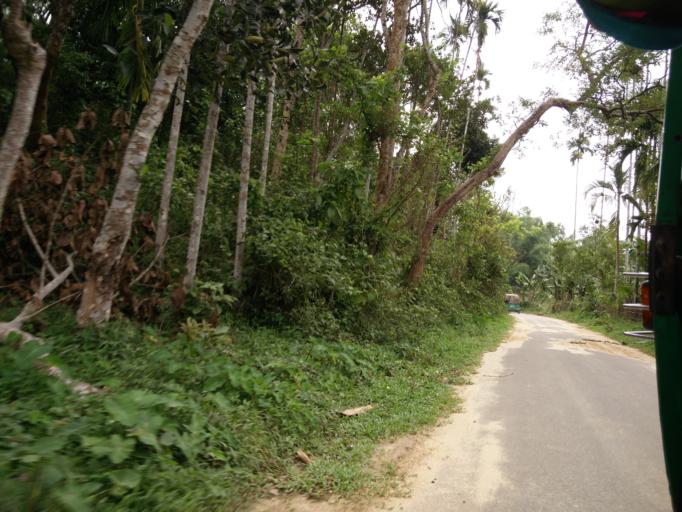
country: IN
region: Tripura
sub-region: Dhalai
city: Kamalpur
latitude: 24.3030
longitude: 91.7876
